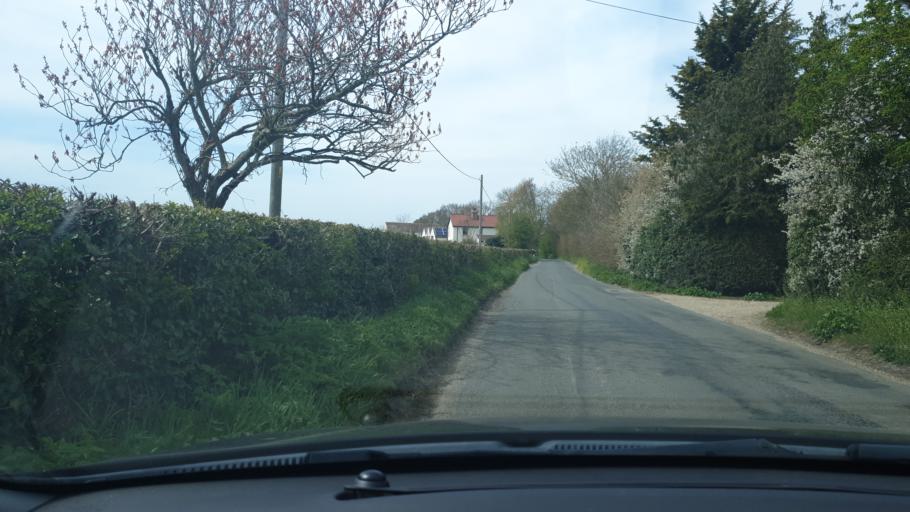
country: GB
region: England
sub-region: Essex
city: Mistley
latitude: 51.9009
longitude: 1.1366
